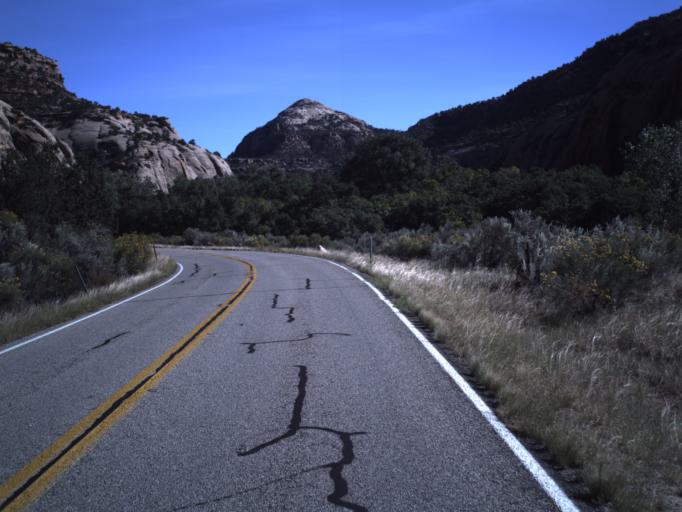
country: US
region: Utah
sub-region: San Juan County
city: Monticello
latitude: 38.0022
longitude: -109.5325
